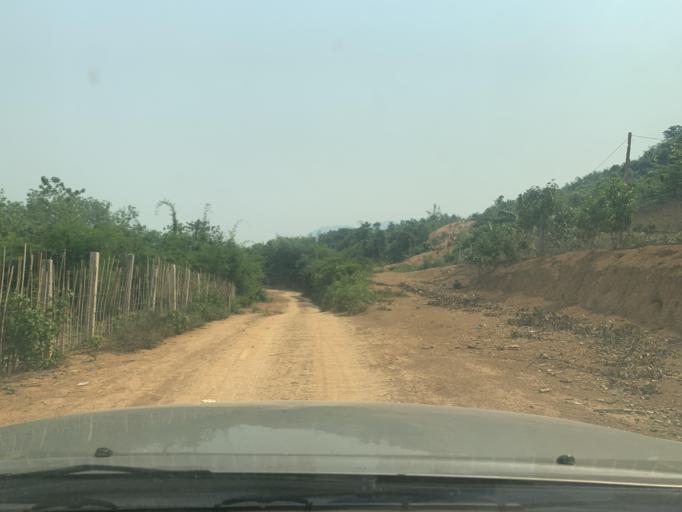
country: LA
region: Louangphabang
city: Xiang Ngeun
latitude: 19.7994
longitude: 102.2016
